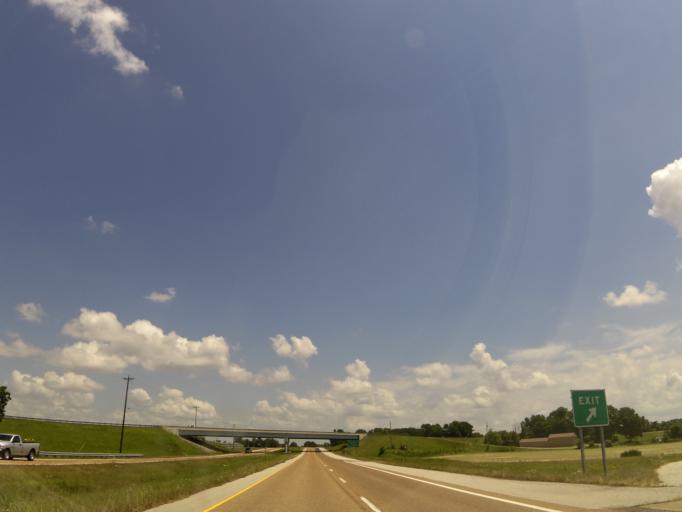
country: US
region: Tennessee
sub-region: Crockett County
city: Alamo
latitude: 35.8197
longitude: -89.1680
